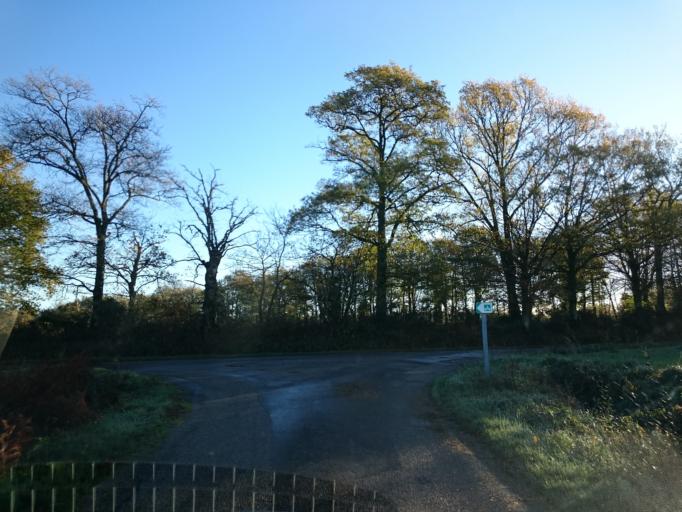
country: FR
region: Brittany
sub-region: Departement d'Ille-et-Vilaine
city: Tresboeuf
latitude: 47.9267
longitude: -1.5563
